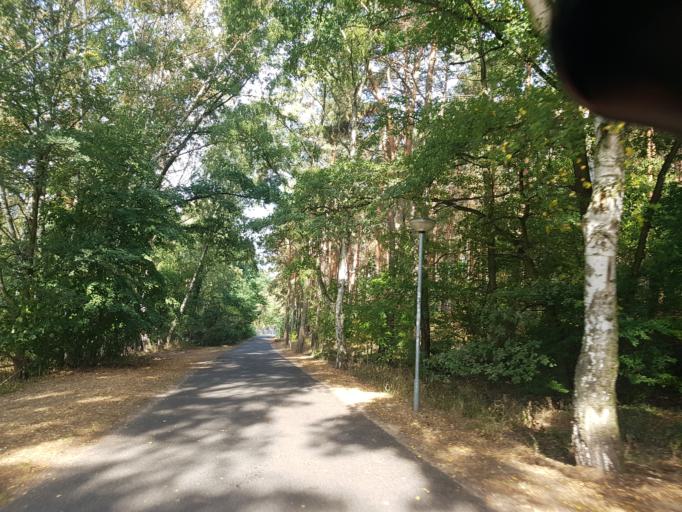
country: DE
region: Brandenburg
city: Belzig
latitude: 52.1483
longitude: 12.5851
